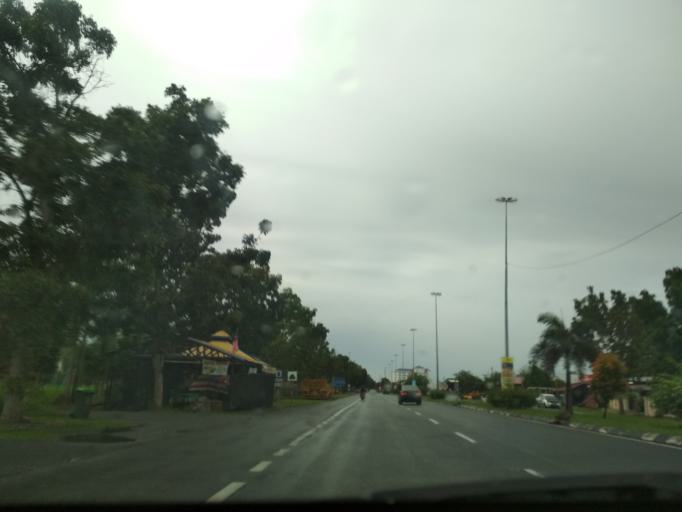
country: MY
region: Perlis
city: Kangar
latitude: 6.4235
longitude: 100.1842
